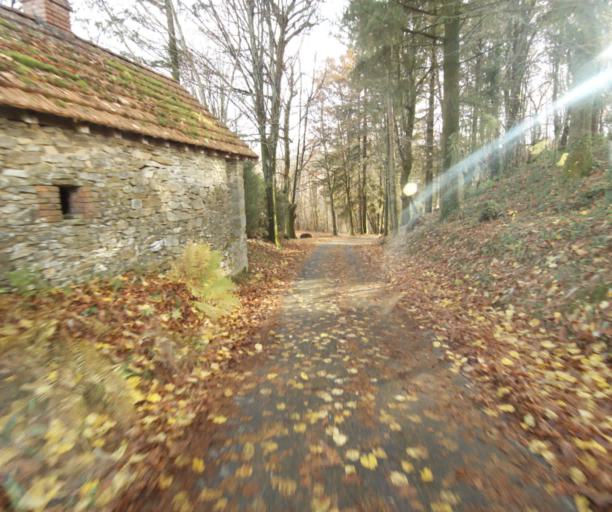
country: FR
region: Limousin
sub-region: Departement de la Correze
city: Sainte-Fortunade
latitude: 45.2031
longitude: 1.7479
